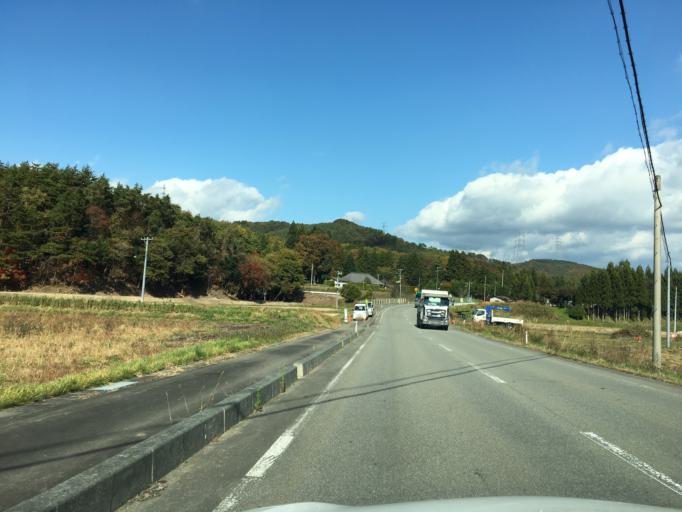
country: JP
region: Fukushima
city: Funehikimachi-funehiki
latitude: 37.3122
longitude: 140.7722
